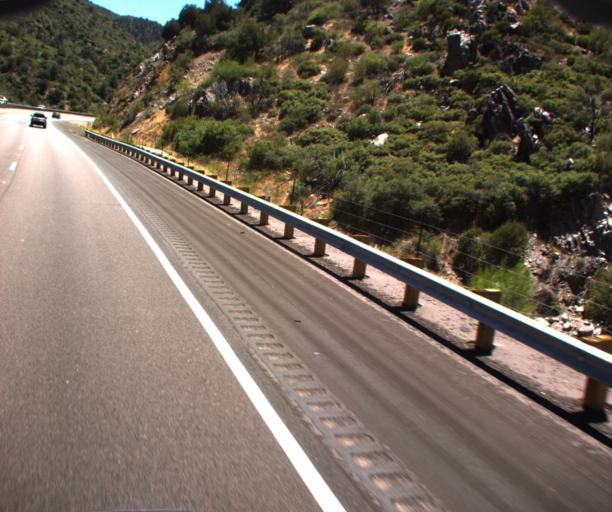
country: US
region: Arizona
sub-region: Gila County
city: Tonto Basin
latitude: 33.9562
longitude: -111.4092
